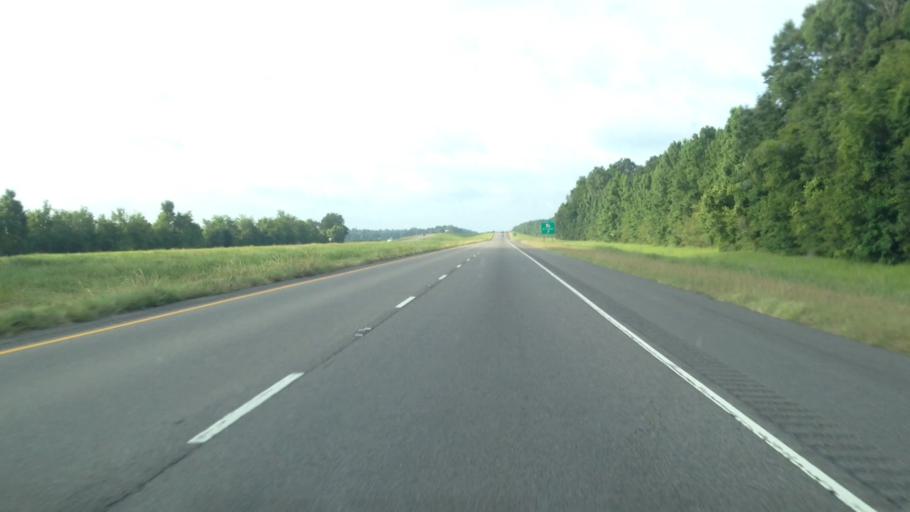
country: US
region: Louisiana
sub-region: Avoyelles Parish
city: Bunkie
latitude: 30.8743
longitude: -92.2279
